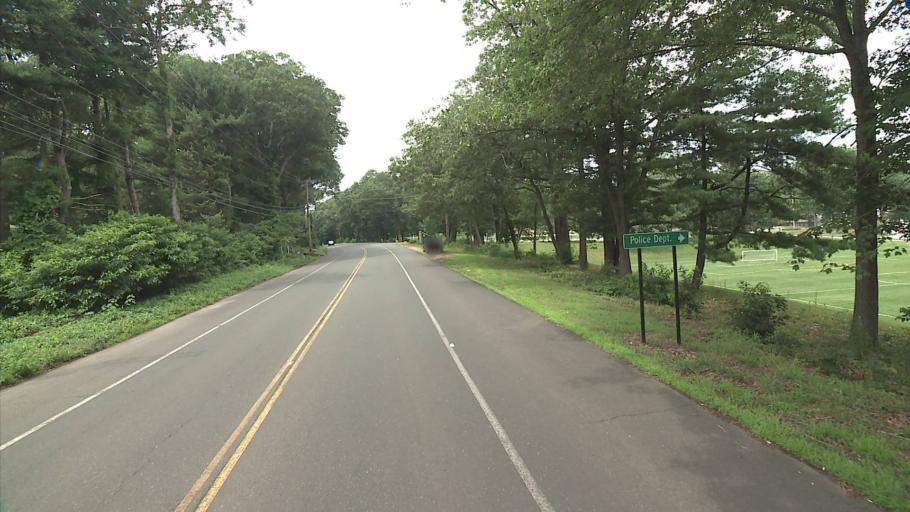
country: US
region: Connecticut
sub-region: New Haven County
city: Madison
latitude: 41.2947
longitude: -72.5757
